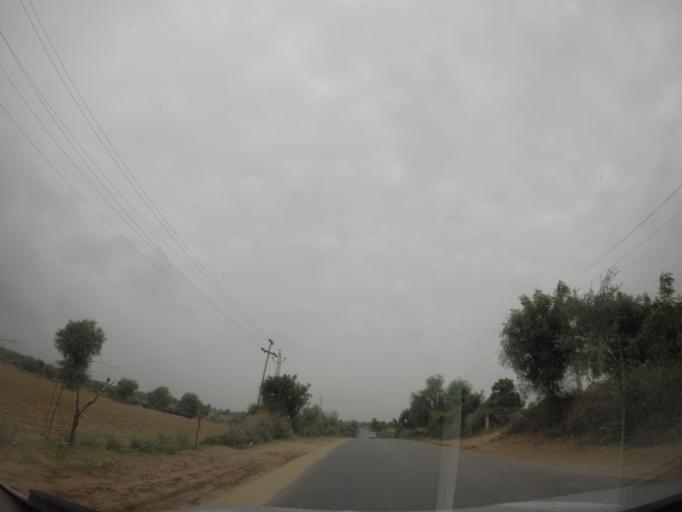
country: IN
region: Rajasthan
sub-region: Jalore
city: Sanchor
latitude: 24.6900
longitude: 71.8308
